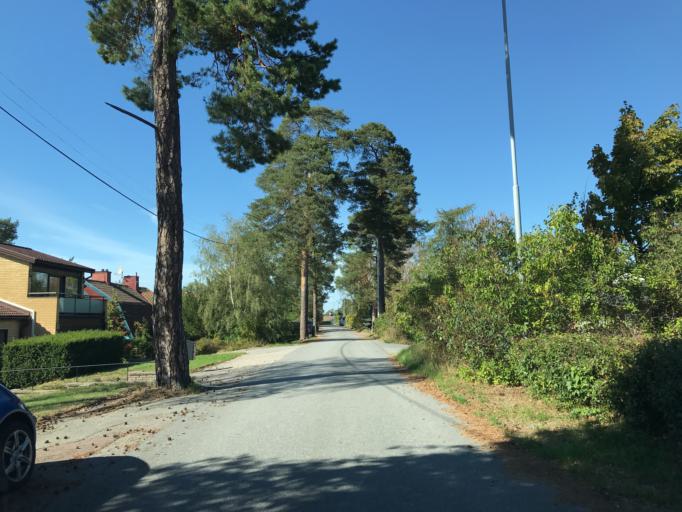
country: SE
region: Stockholm
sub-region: Sollentuna Kommun
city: Sollentuna
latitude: 59.4234
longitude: 17.9672
